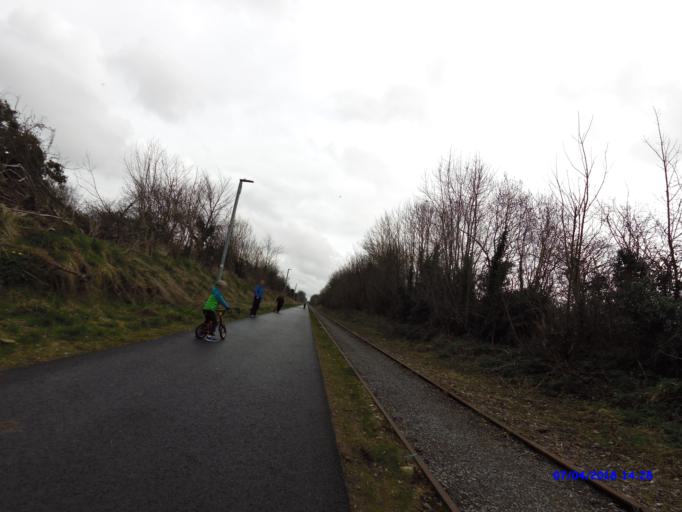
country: IE
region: Leinster
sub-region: An Iarmhi
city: Athlone
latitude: 53.4249
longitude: -7.9136
